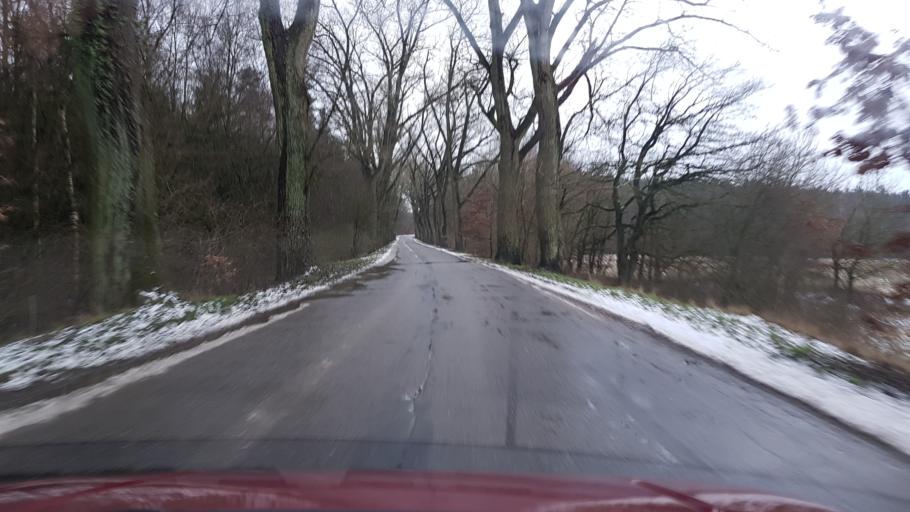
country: PL
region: West Pomeranian Voivodeship
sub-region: Powiat goleniowski
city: Nowogard
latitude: 53.6374
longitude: 15.1216
